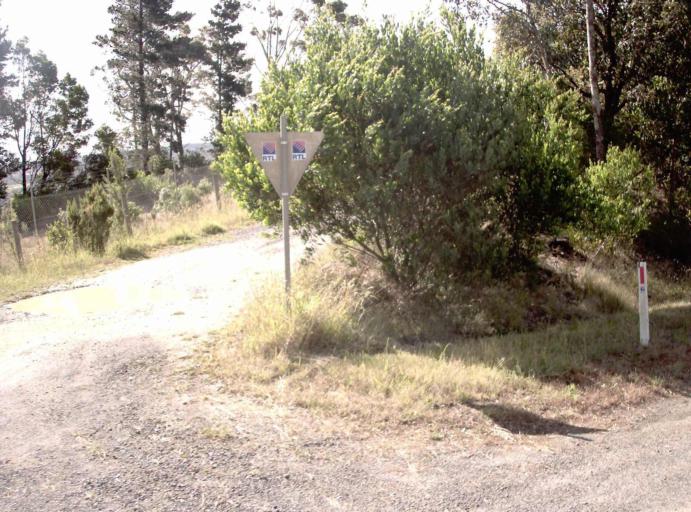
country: AU
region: Victoria
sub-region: Latrobe
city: Morwell
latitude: -38.1838
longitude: 146.4041
